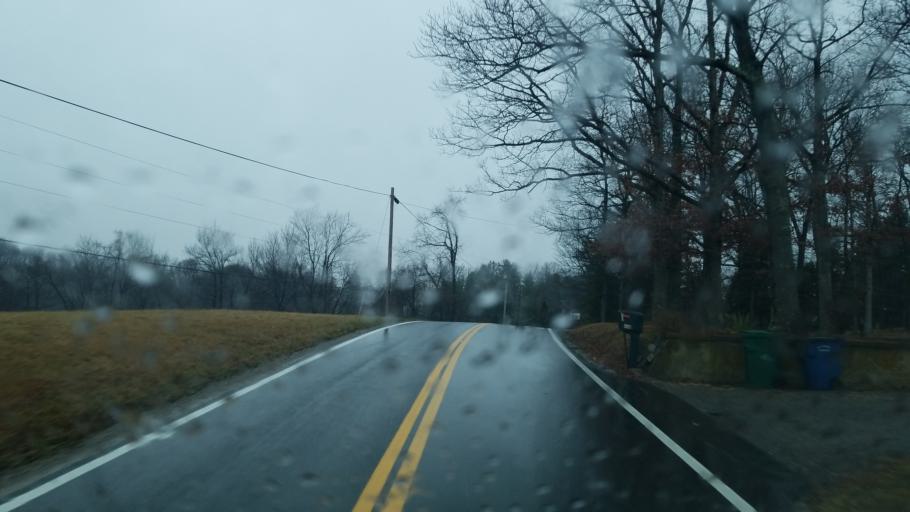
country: US
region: Ohio
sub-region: Licking County
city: Newark
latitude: 40.0927
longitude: -82.3547
